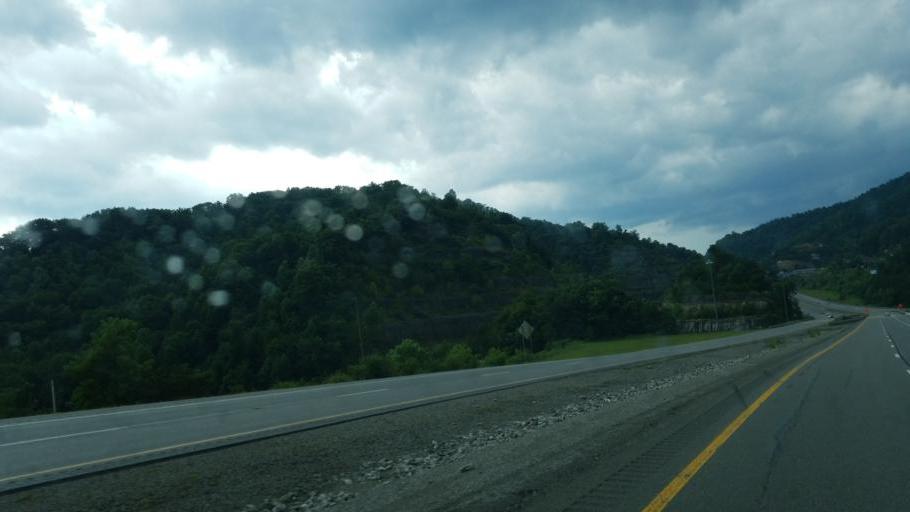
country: US
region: Kentucky
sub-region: Pike County
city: Pikeville
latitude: 37.5130
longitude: -82.4714
